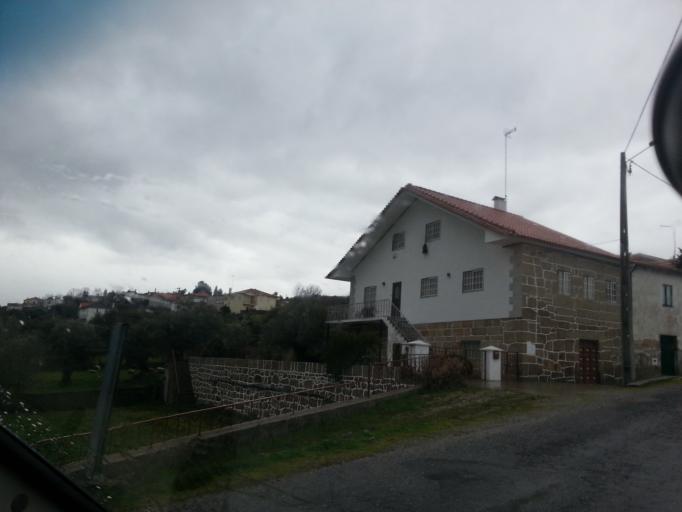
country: PT
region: Guarda
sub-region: Celorico da Beira
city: Celorico da Beira
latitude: 40.6290
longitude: -7.4347
